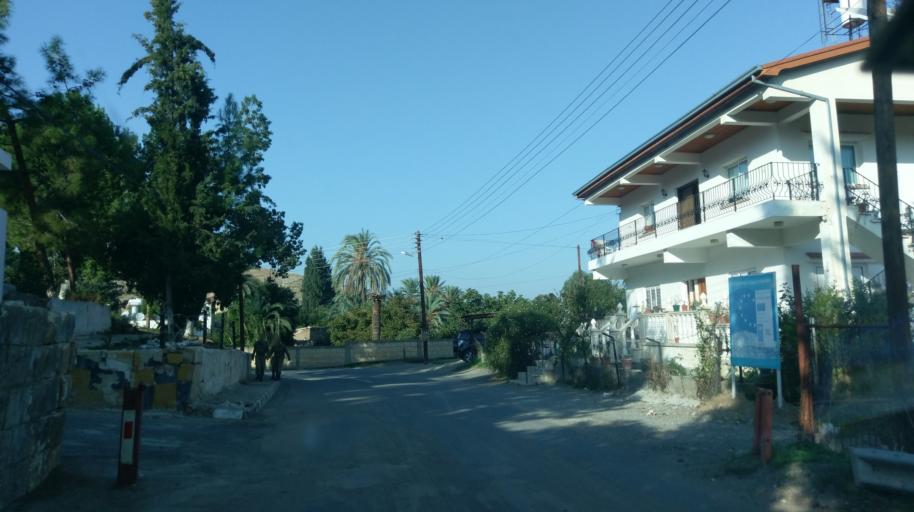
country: CY
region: Lefkosia
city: Lefka
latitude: 35.0901
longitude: 32.8433
